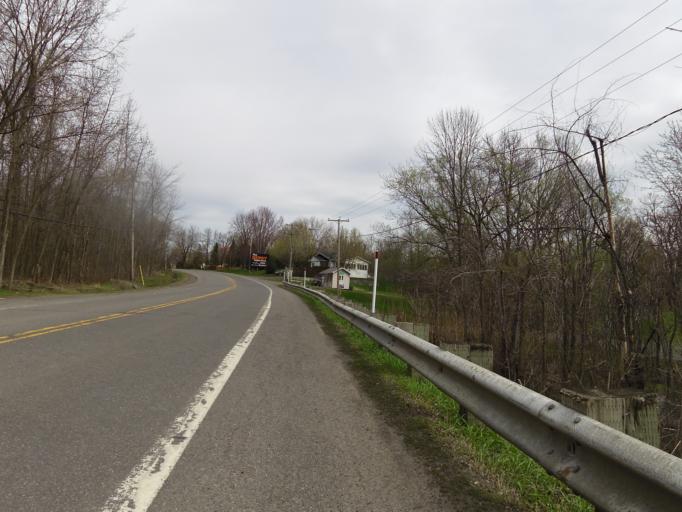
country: CA
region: Quebec
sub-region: Monteregie
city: Hudson
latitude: 45.4919
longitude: -74.1323
